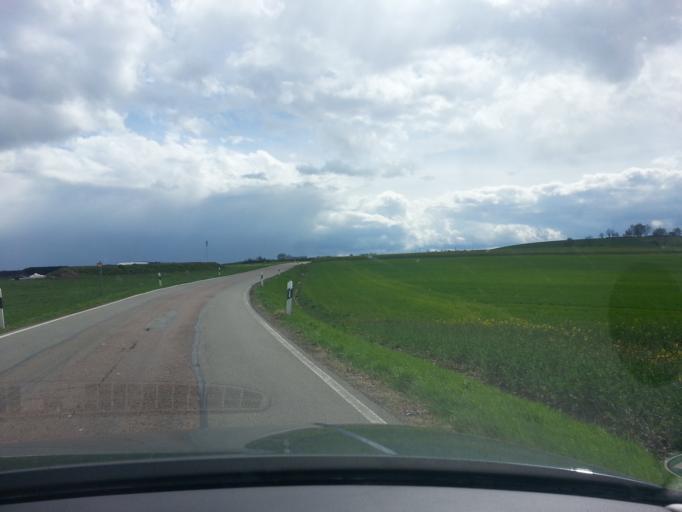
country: DE
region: Rheinland-Pfalz
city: Schmitshausen
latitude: 49.2892
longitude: 7.5224
